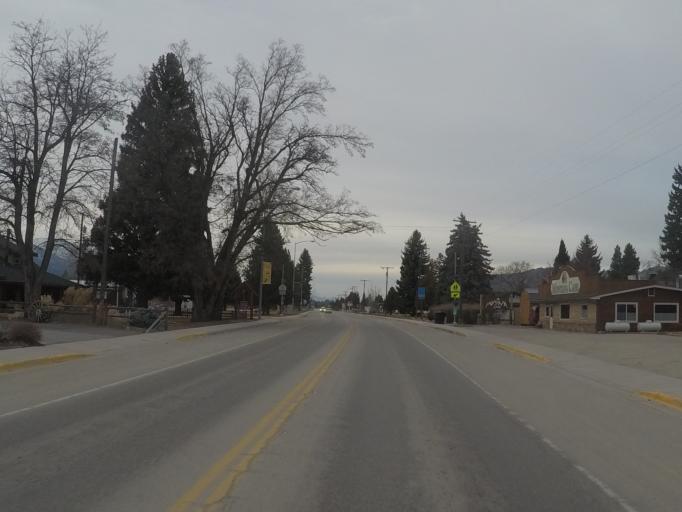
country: US
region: Montana
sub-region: Ravalli County
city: Hamilton
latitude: 46.0257
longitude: -114.1776
